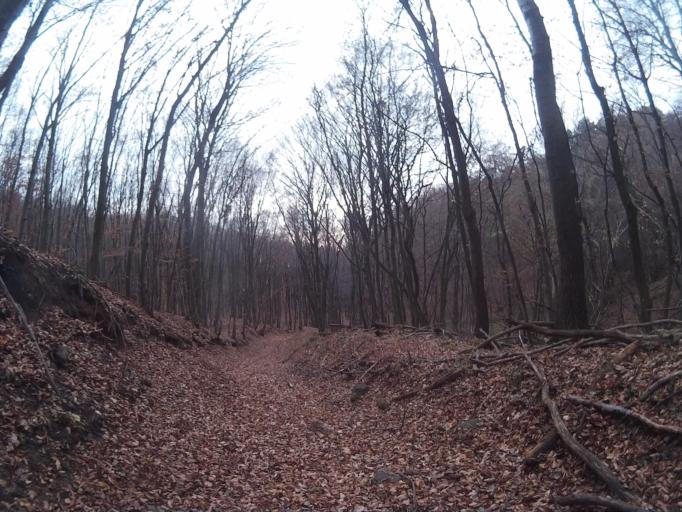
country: HU
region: Veszprem
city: Tapolca
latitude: 46.9467
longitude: 17.4955
